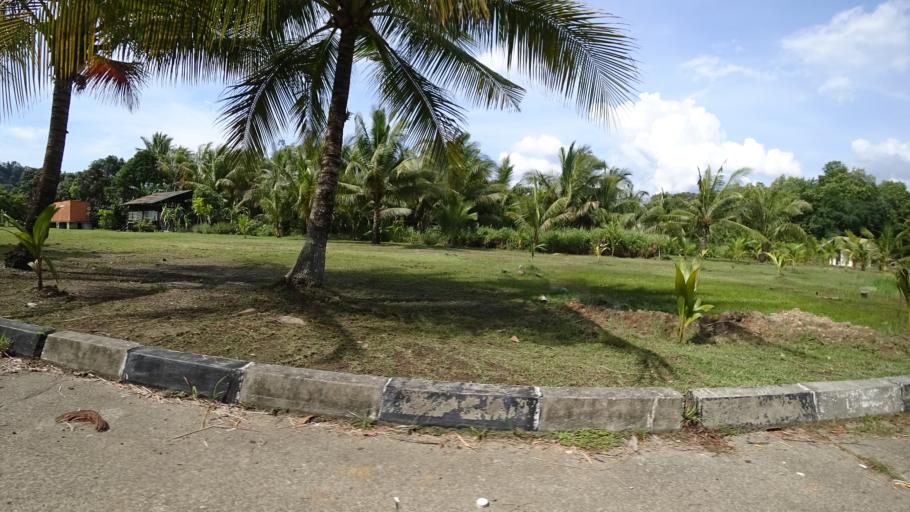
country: BN
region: Brunei and Muara
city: Bandar Seri Begawan
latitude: 4.8485
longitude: 114.8888
